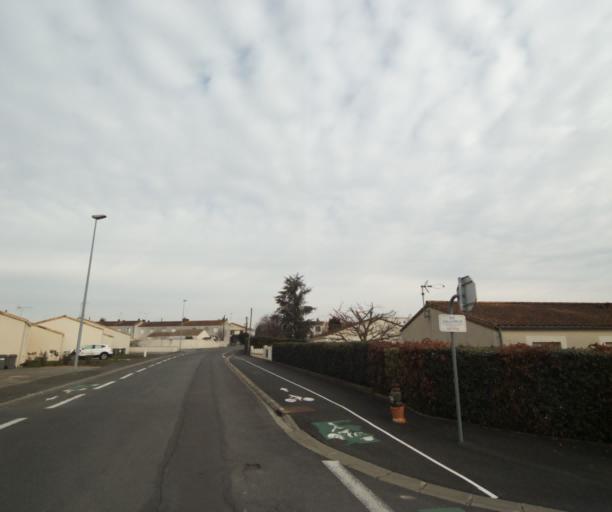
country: FR
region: Poitou-Charentes
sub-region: Departement des Deux-Sevres
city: Niort
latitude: 46.3079
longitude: -0.4522
